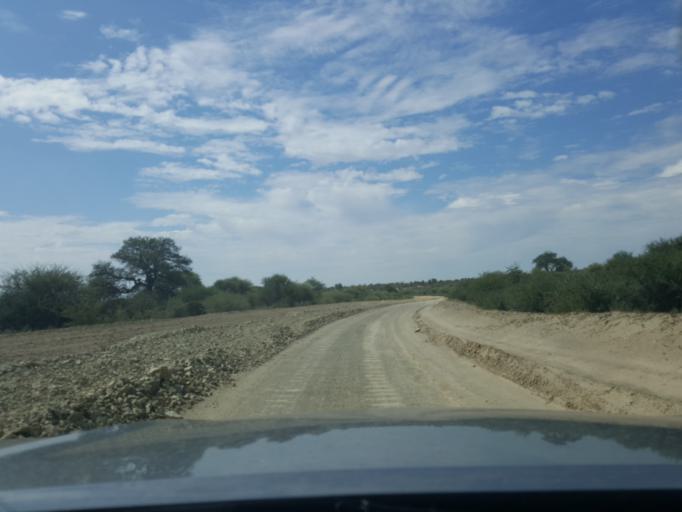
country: BW
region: Kweneng
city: Letlhakeng
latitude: -23.9935
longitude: 24.9712
